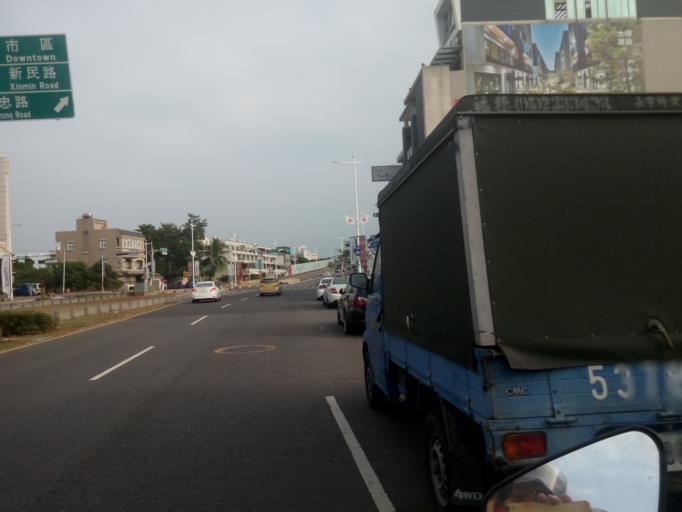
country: TW
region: Taiwan
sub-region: Chiayi
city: Jiayi Shi
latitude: 23.4776
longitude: 120.4299
